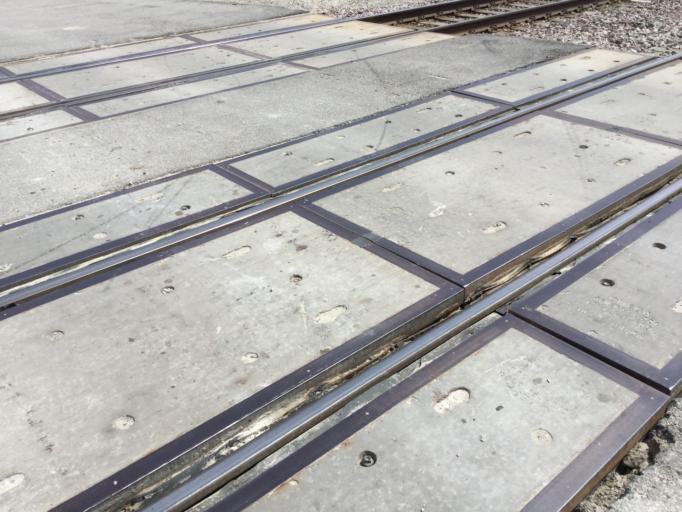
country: US
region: Kansas
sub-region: Johnson County
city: Spring Hill
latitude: 38.7819
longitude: -94.8159
